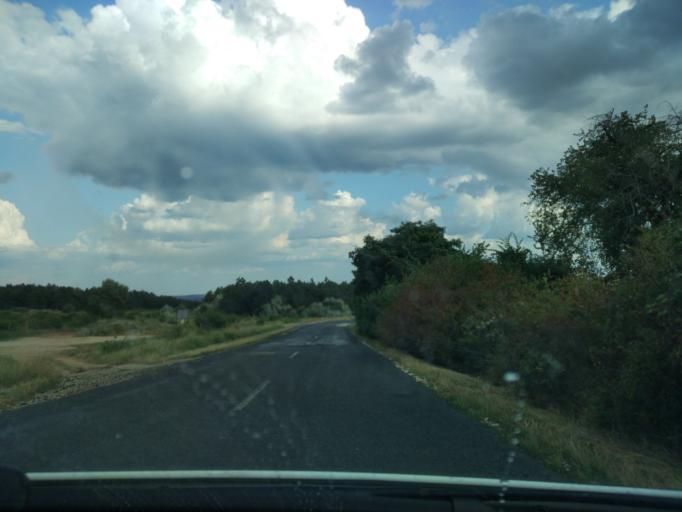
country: HU
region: Veszprem
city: Varpalota
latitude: 47.2192
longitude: 18.1484
